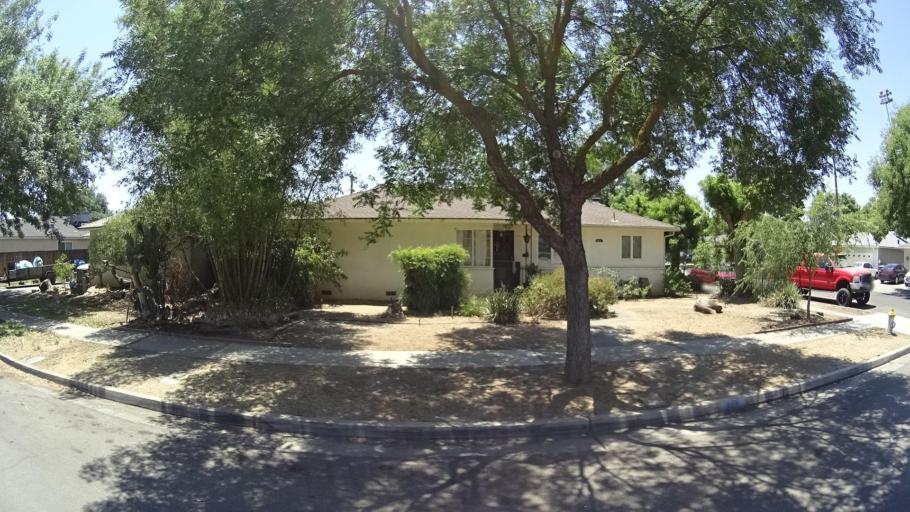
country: US
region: California
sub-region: Fresno County
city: Fresno
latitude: 36.8004
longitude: -119.7671
